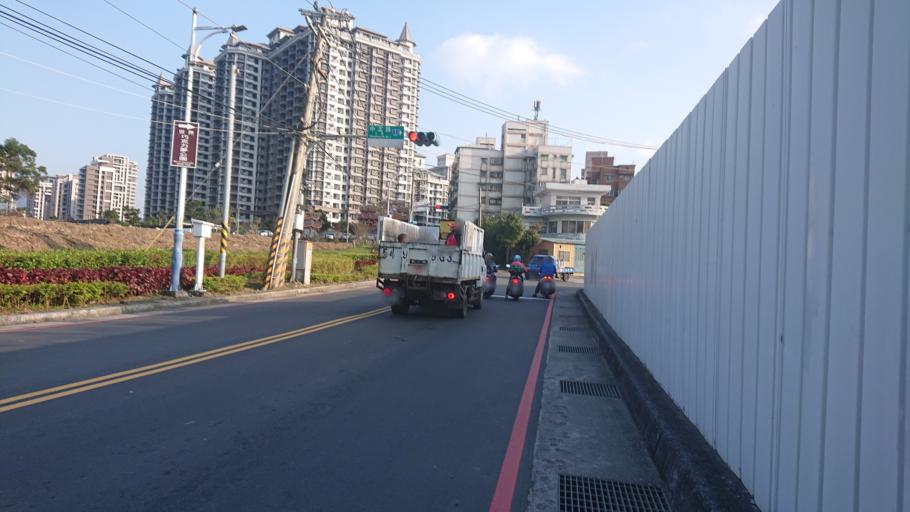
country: TW
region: Taipei
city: Taipei
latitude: 25.1901
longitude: 121.4263
